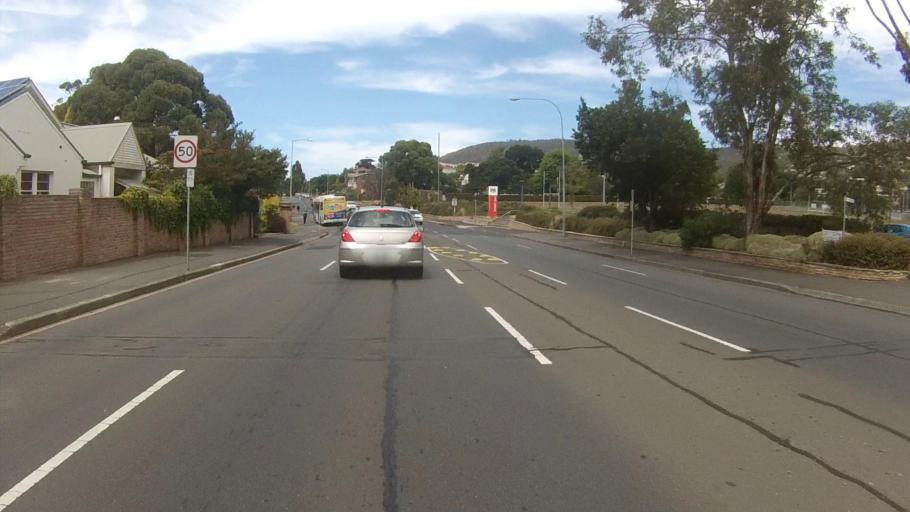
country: AU
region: Tasmania
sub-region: Hobart
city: Sandy Bay
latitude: -42.8994
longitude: 147.3304
